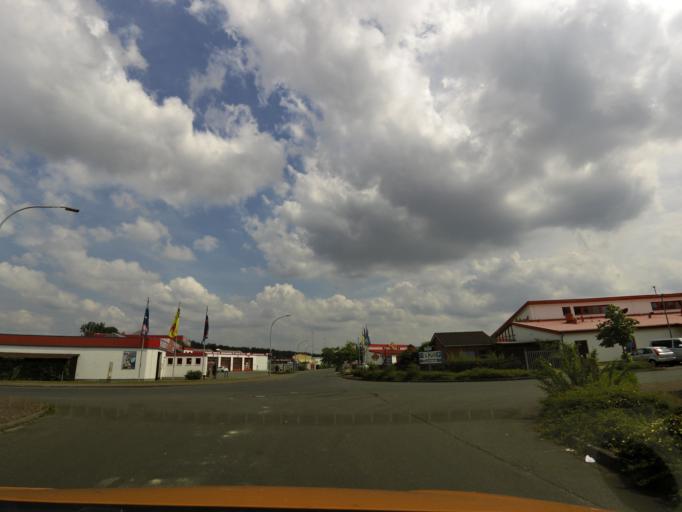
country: DE
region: Mecklenburg-Vorpommern
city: Neustadt-Glewe
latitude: 53.3808
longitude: 11.6266
